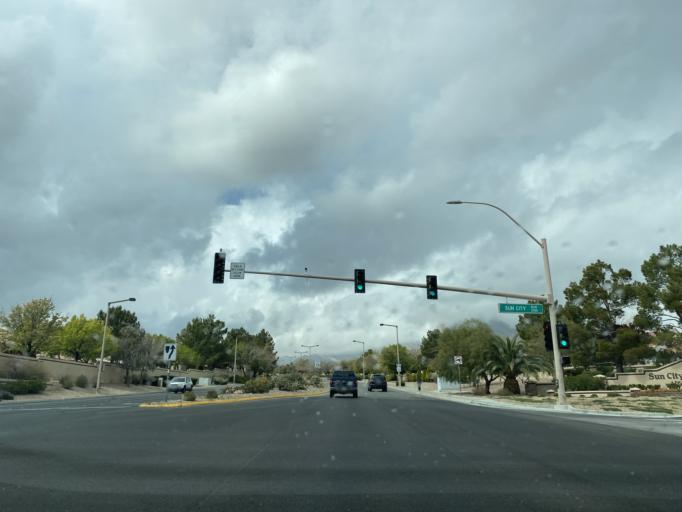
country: US
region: Nevada
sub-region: Clark County
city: Summerlin South
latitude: 36.2052
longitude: -115.3201
